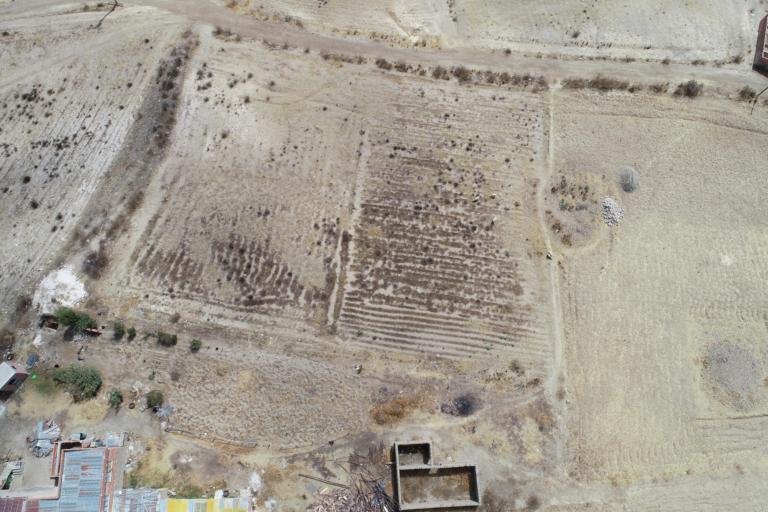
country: BO
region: La Paz
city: La Paz
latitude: -16.6007
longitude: -68.1296
